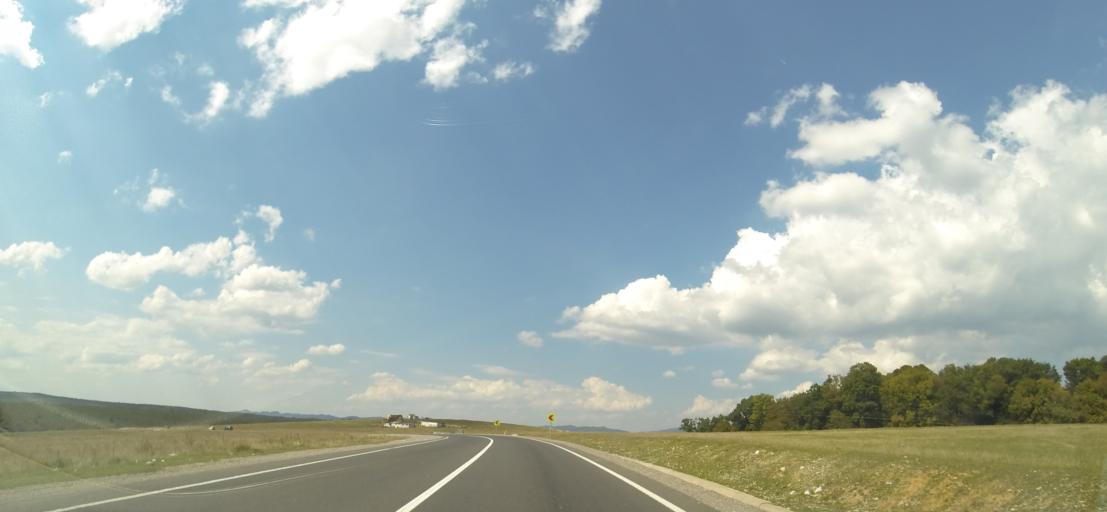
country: RO
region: Brasov
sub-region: Comuna Dumbravita
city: Dumbravita
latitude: 45.7500
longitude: 25.4049
